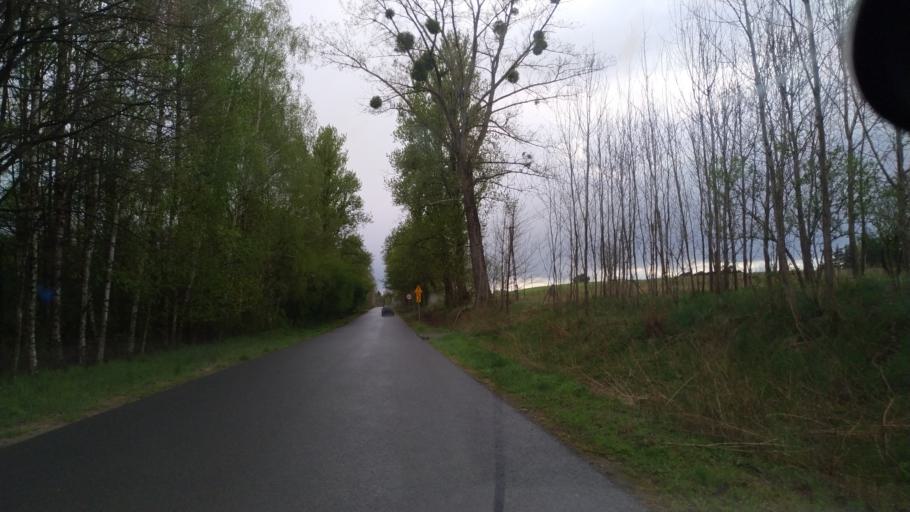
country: PL
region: Pomeranian Voivodeship
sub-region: Powiat starogardzki
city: Osiek
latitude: 53.6415
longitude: 18.4846
